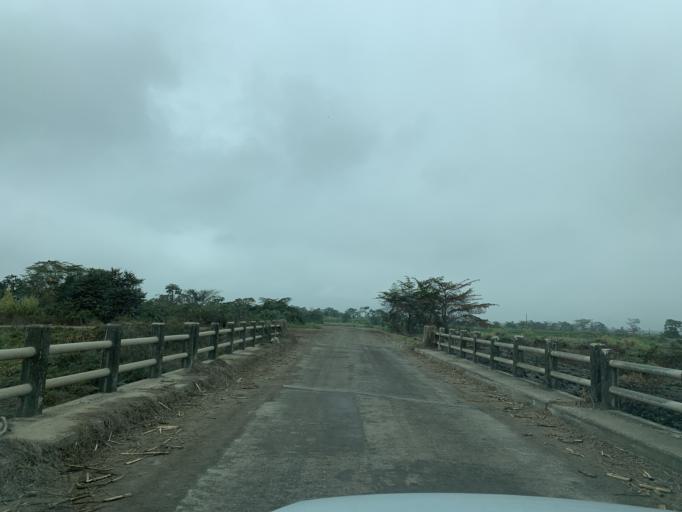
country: EC
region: Guayas
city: Coronel Marcelino Mariduena
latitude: -2.3588
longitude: -79.5829
